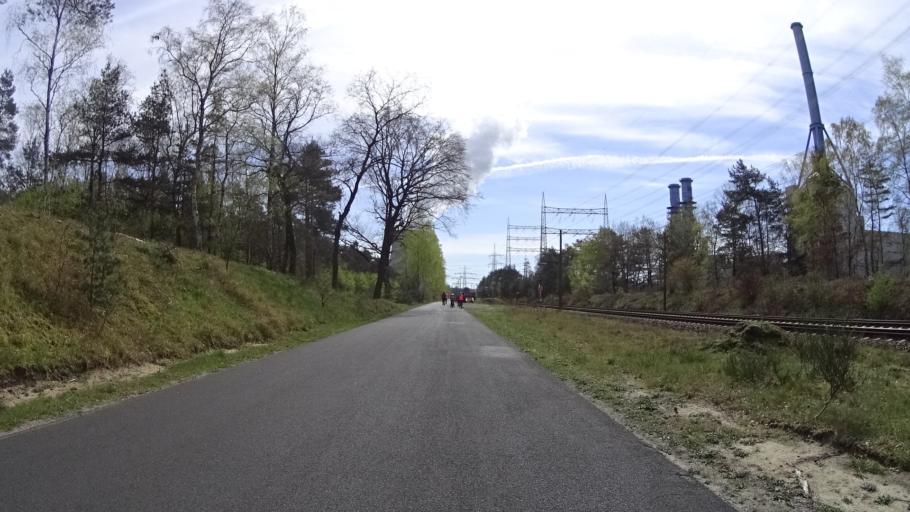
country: DE
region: Lower Saxony
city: Lingen
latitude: 52.4827
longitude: 7.3078
